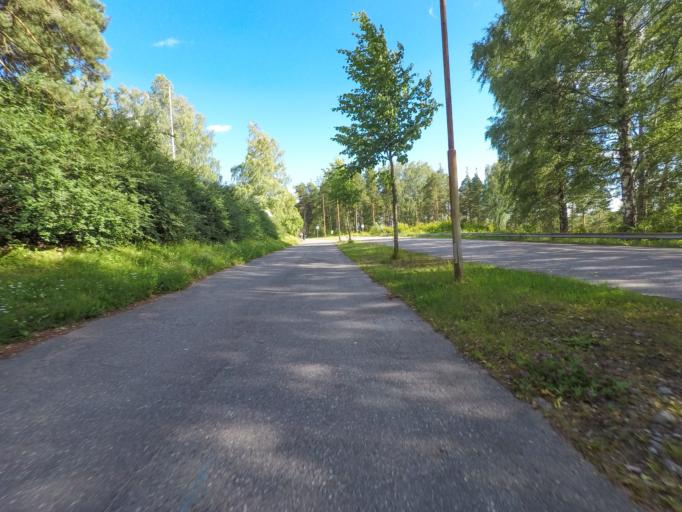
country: FI
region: South Karelia
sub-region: Lappeenranta
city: Lappeenranta
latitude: 61.0669
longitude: 28.1577
